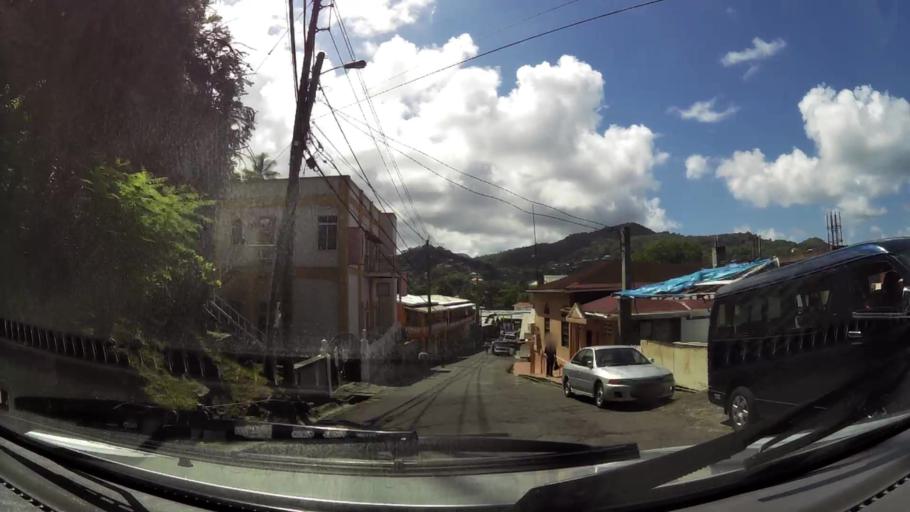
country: GD
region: Saint Patrick
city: Sauteurs
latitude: 12.2249
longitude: -61.6409
